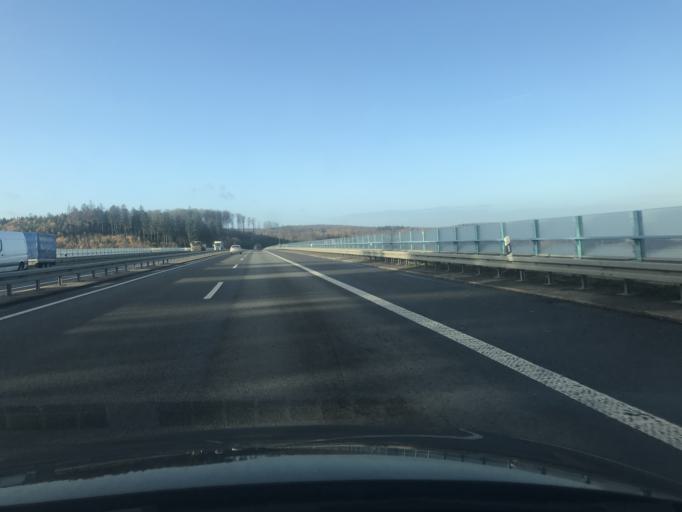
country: DE
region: North Rhine-Westphalia
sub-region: Regierungsbezirk Arnsberg
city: Arnsberg
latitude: 51.3838
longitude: 8.1366
